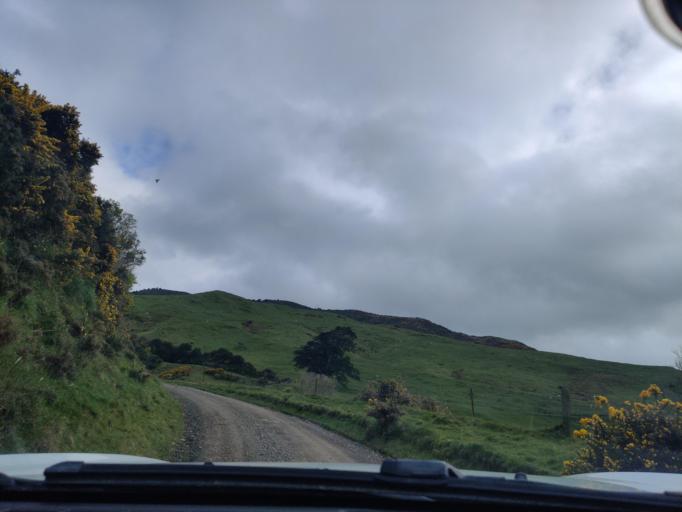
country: NZ
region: Manawatu-Wanganui
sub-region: Palmerston North City
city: Palmerston North
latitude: -40.2801
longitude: 175.8569
